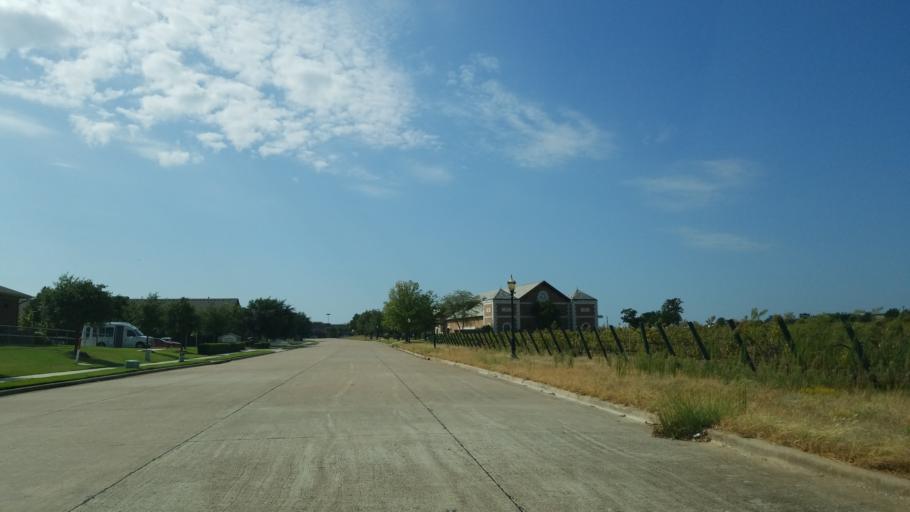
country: US
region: Texas
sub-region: Tarrant County
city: Grapevine
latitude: 32.8875
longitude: -97.0967
